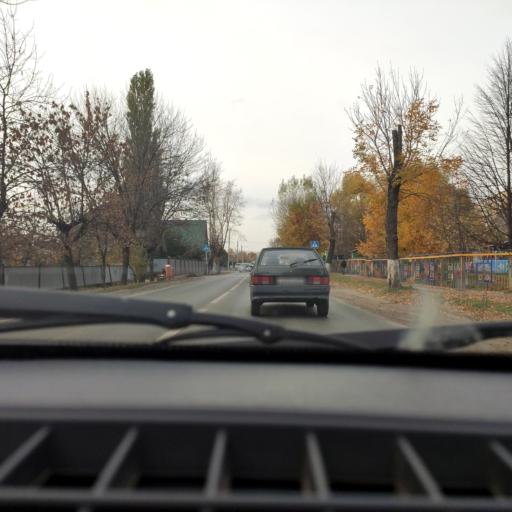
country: RU
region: Bashkortostan
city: Avdon
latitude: 54.6985
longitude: 55.8243
